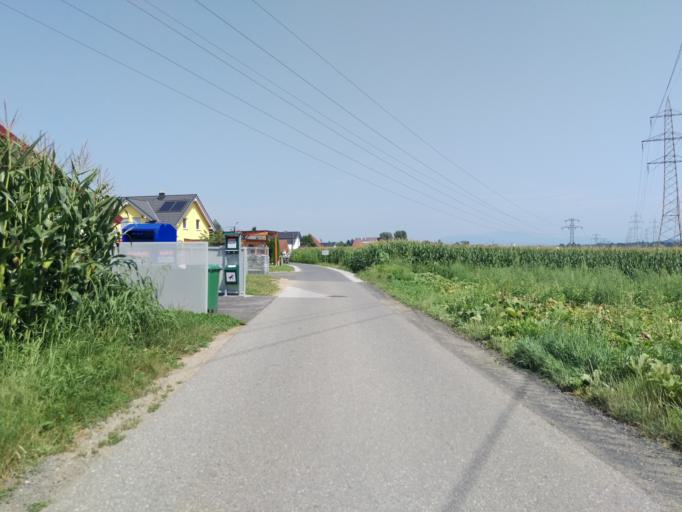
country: AT
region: Styria
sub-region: Politischer Bezirk Graz-Umgebung
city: Werndorf
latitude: 46.9354
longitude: 15.4890
